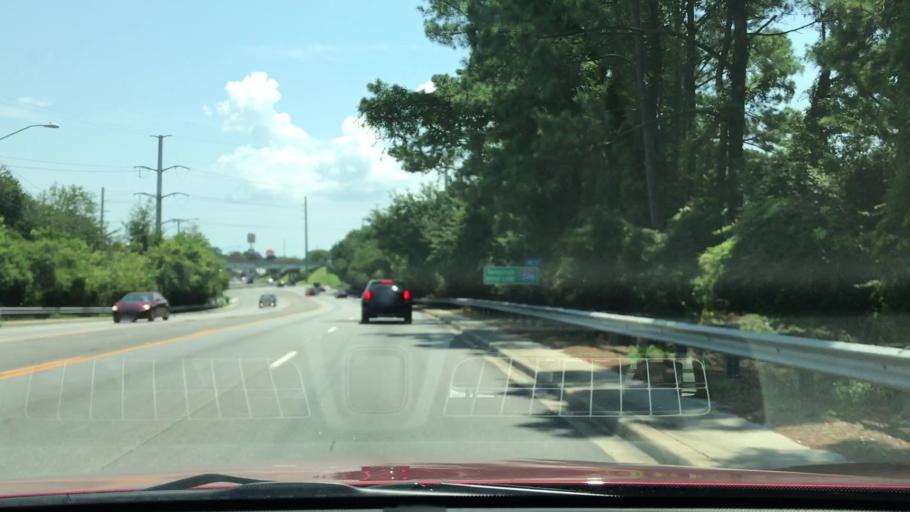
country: US
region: South Carolina
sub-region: Charleston County
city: North Charleston
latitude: 32.8554
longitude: -80.0244
